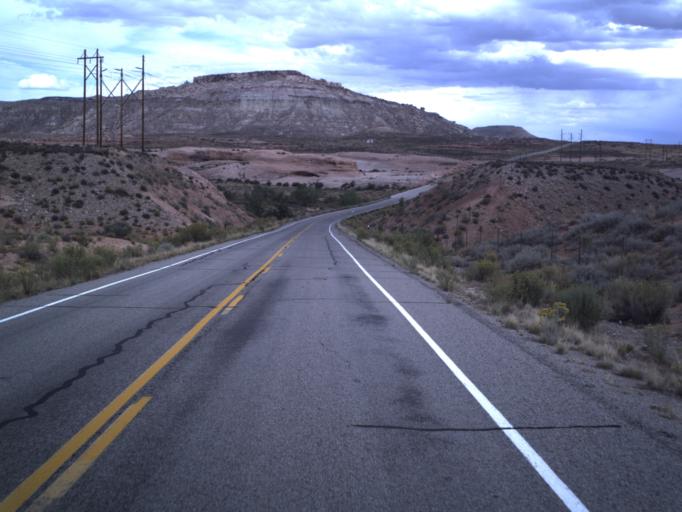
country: US
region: Utah
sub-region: San Juan County
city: Blanding
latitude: 37.2990
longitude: -109.4619
